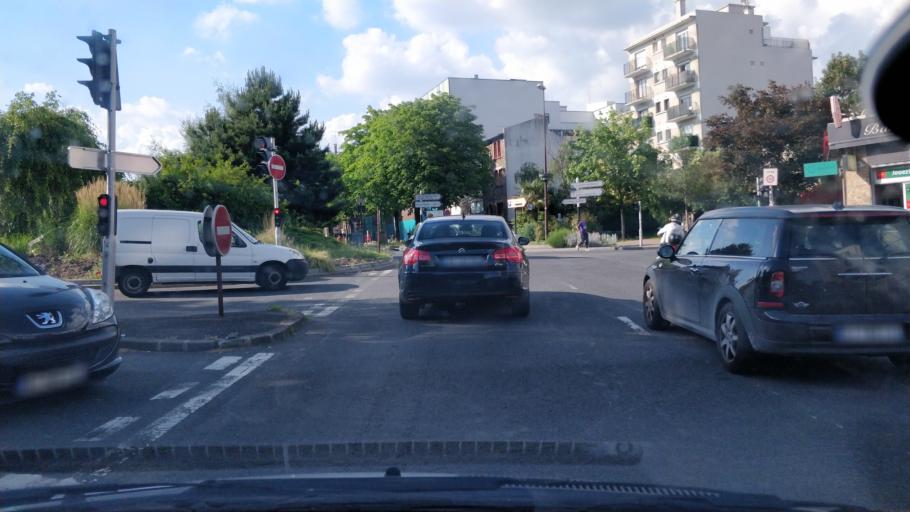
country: FR
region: Ile-de-France
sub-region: Departement de Seine-Saint-Denis
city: Montreuil
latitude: 48.8672
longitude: 2.4346
